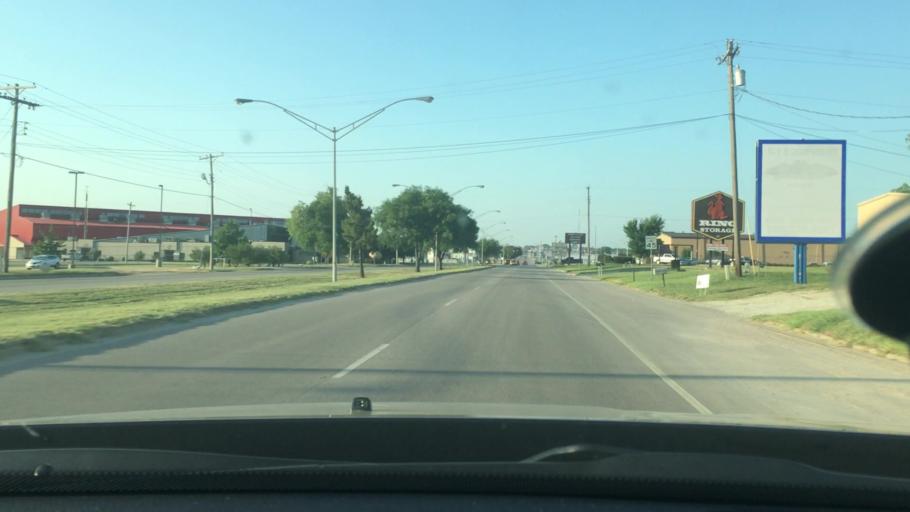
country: US
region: Oklahoma
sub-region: Pontotoc County
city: Ada
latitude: 34.7939
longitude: -96.6788
